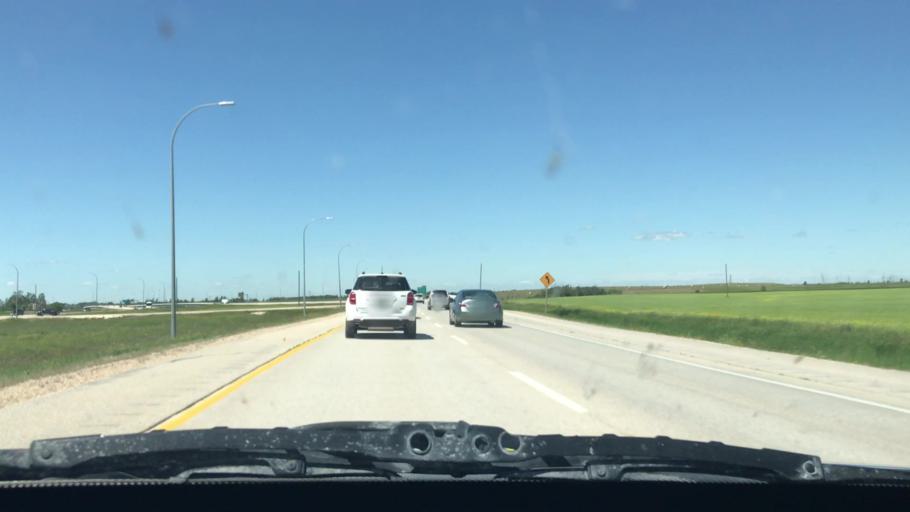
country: CA
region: Manitoba
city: Winnipeg
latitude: 49.8251
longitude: -96.9451
